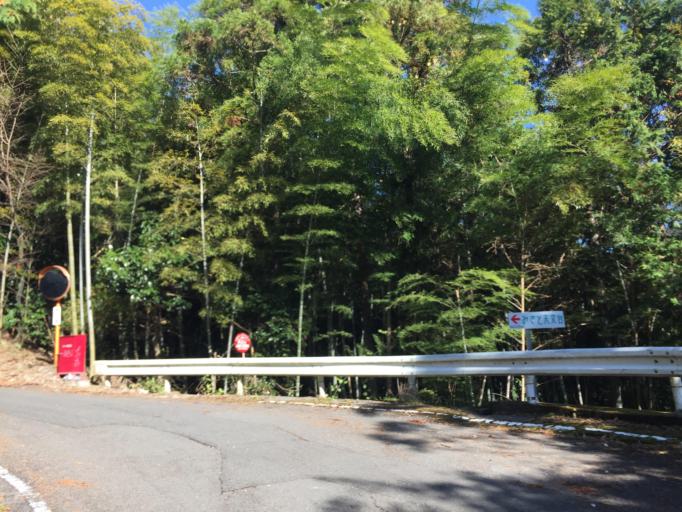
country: JP
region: Wakayama
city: Iwade
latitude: 34.1448
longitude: 135.4154
